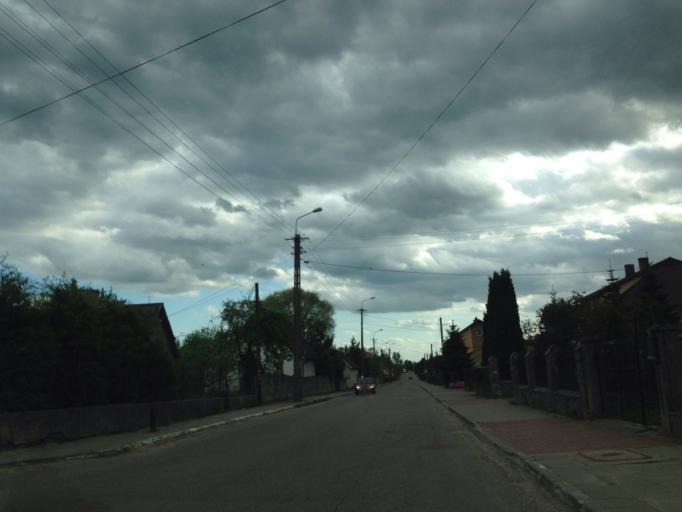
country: PL
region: Podlasie
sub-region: Powiat lomzynski
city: Wizna
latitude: 53.1945
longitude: 22.3822
